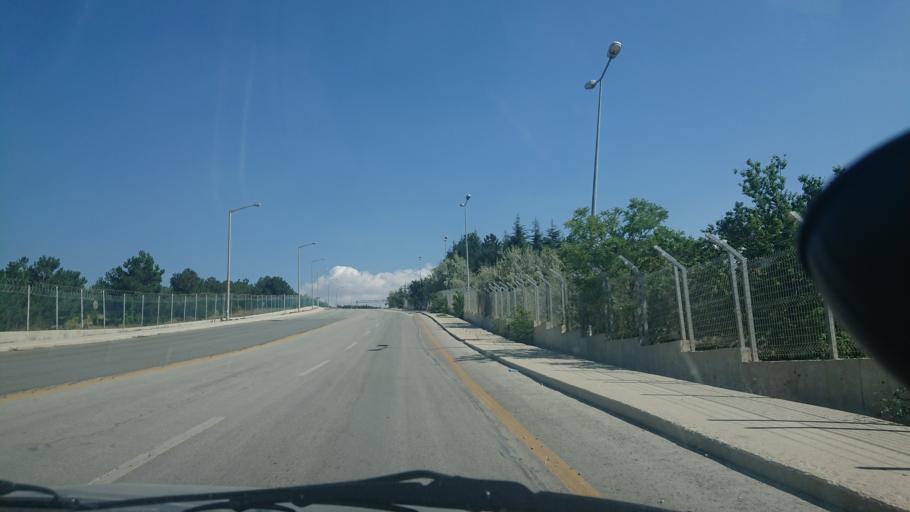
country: TR
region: Ankara
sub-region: Goelbasi
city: Golbasi
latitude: 39.8071
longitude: 32.8251
